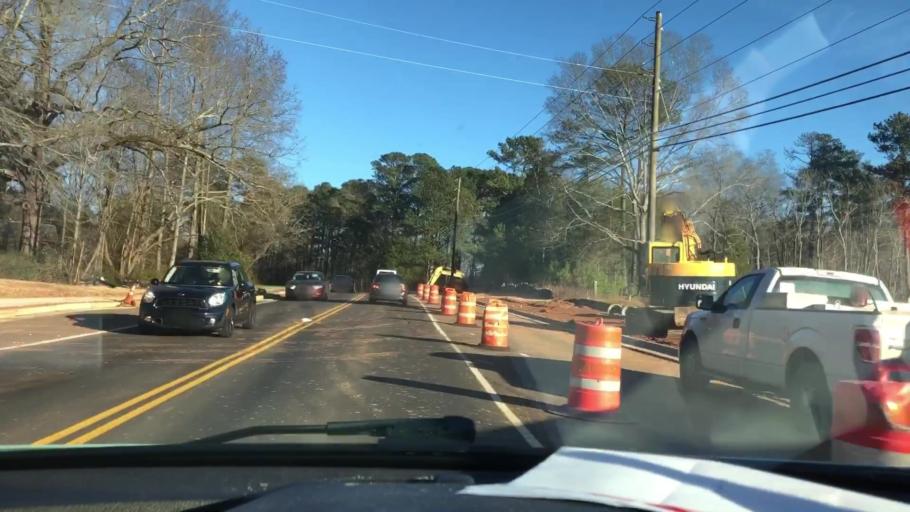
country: US
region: Georgia
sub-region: Gwinnett County
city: Snellville
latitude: 33.8755
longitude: -84.0734
